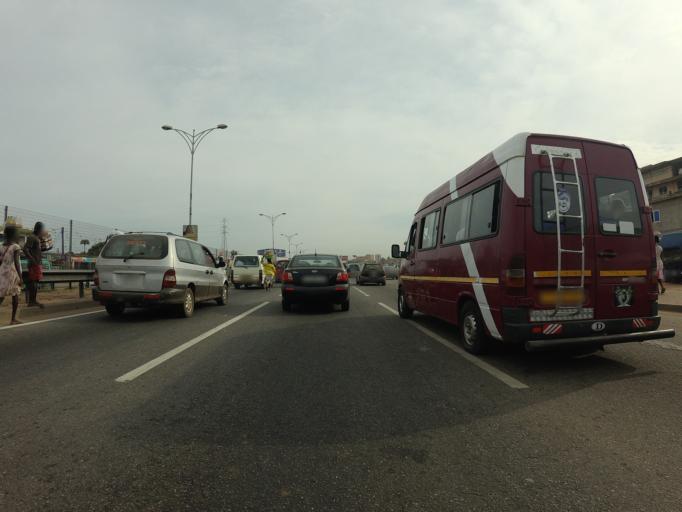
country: GH
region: Greater Accra
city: Gbawe
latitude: 5.5830
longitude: -0.2750
